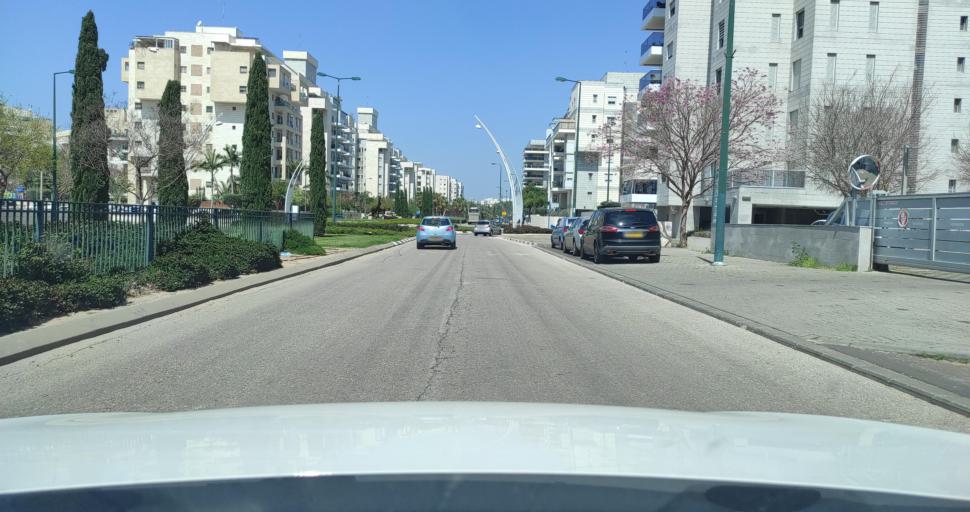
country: IL
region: Central District
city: Nordiyya
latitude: 32.2970
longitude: 34.8735
